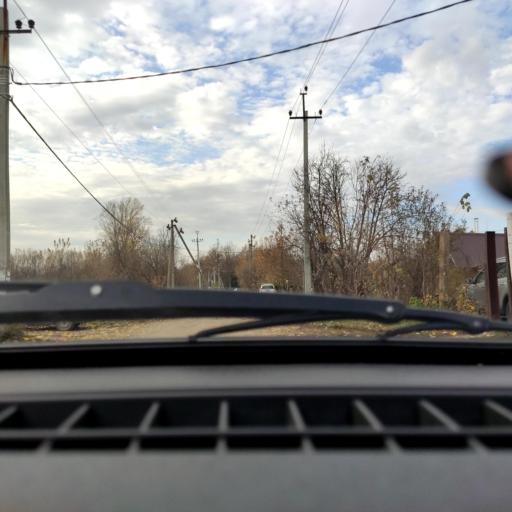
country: RU
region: Bashkortostan
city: Ufa
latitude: 54.7722
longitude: 55.9317
